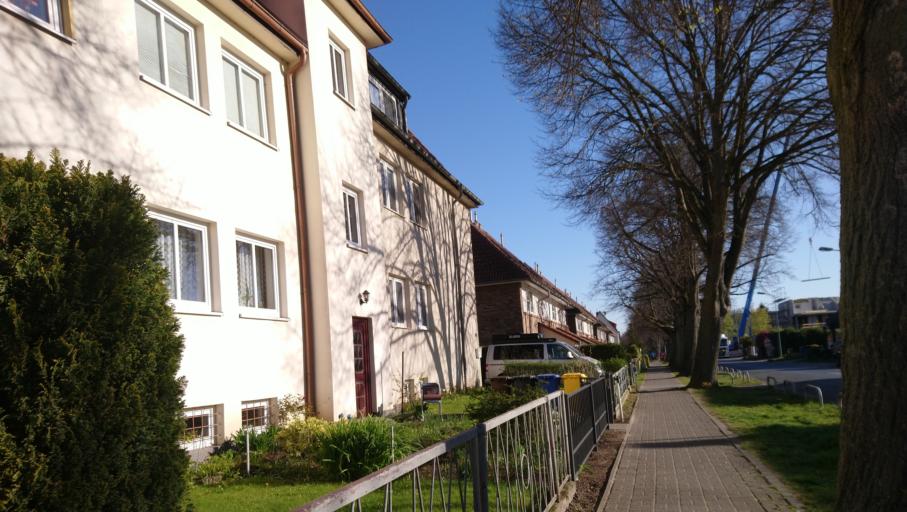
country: DE
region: Mecklenburg-Vorpommern
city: Rostock
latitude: 54.0678
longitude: 12.1338
